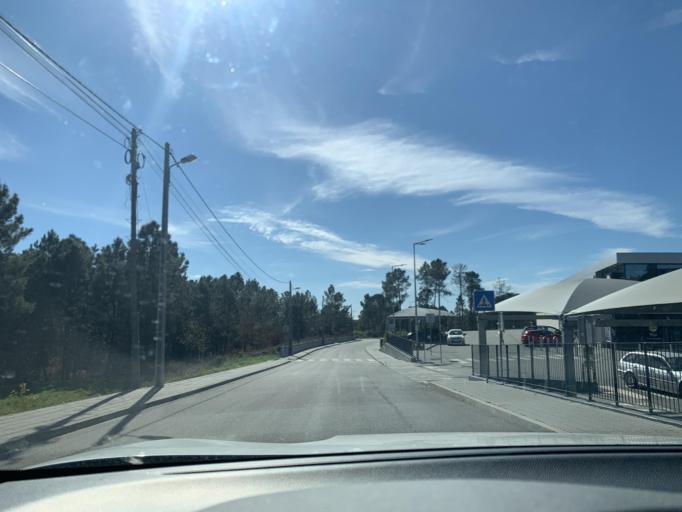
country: PT
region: Viseu
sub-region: Viseu
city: Viseu
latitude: 40.6329
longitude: -7.9307
